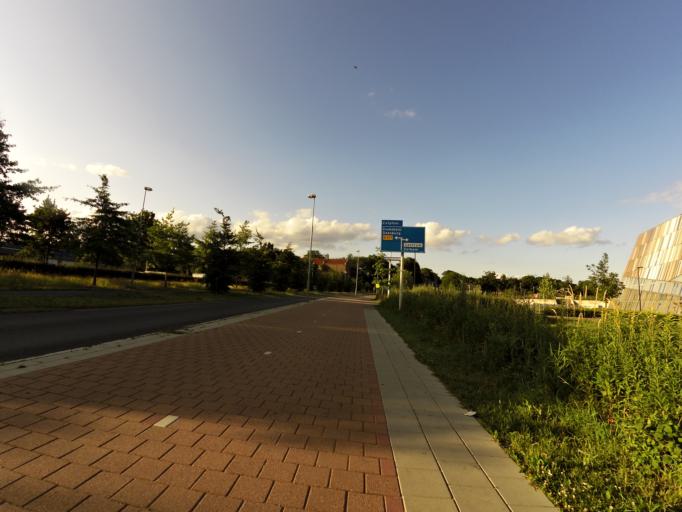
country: NL
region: Gelderland
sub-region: Gemeente Doetinchem
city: Doetinchem
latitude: 51.9707
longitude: 6.2745
